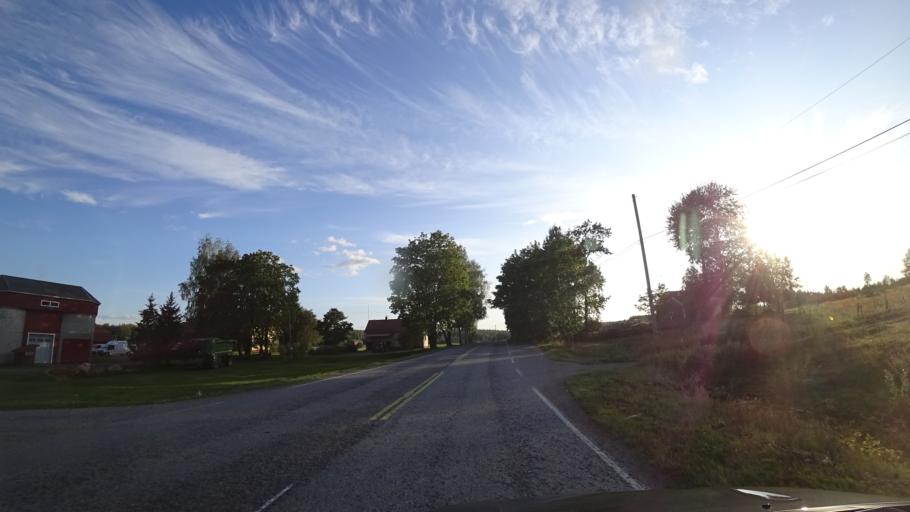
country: FI
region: Haeme
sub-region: Haemeenlinna
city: Lammi
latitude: 61.0437
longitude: 24.9383
